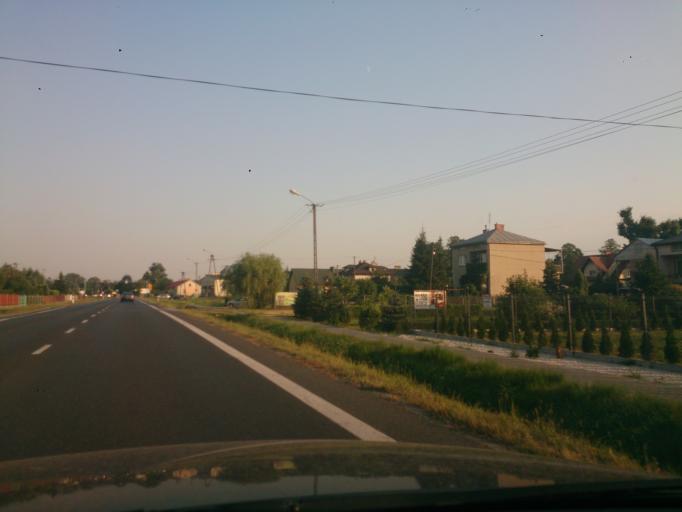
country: PL
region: Subcarpathian Voivodeship
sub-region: Powiat kolbuszowski
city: Kolbuszowa
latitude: 50.2288
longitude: 21.7912
